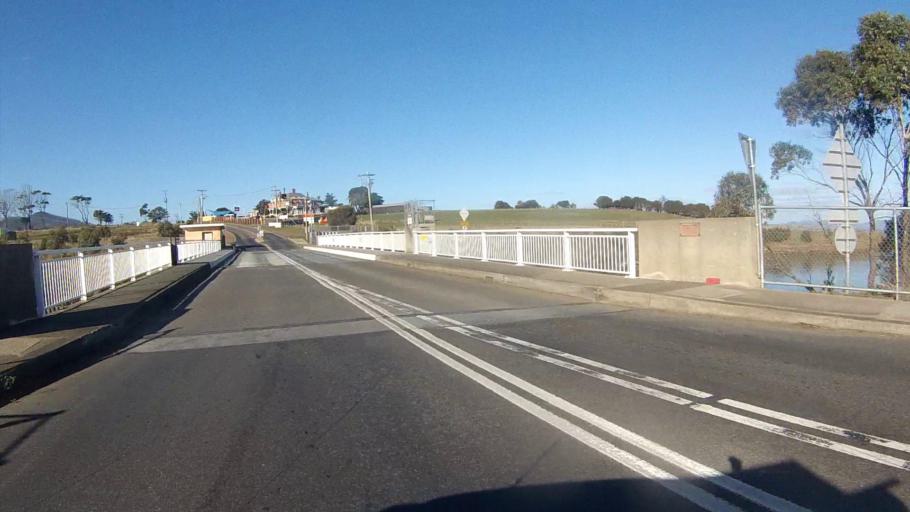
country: AU
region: Tasmania
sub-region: Sorell
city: Sorell
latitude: -42.8903
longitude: 147.8054
